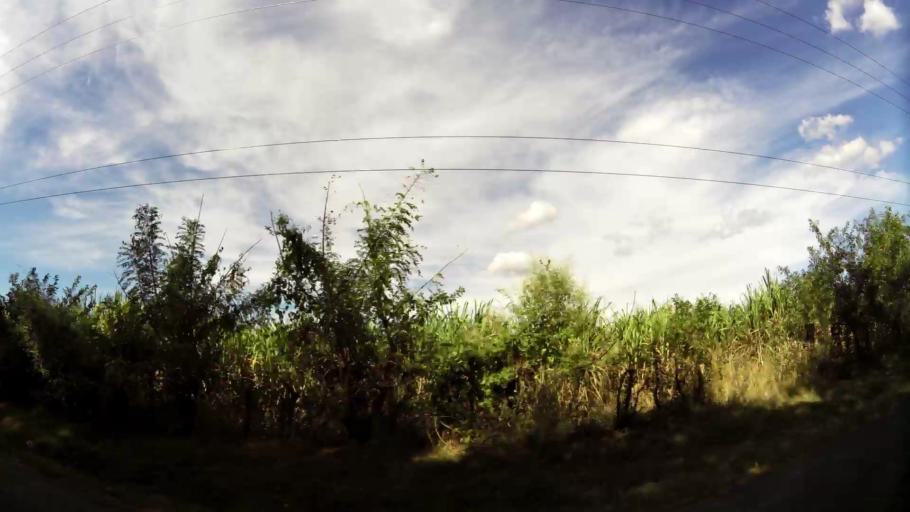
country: SV
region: San Salvador
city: Aguilares
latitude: 13.9581
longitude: -89.1492
